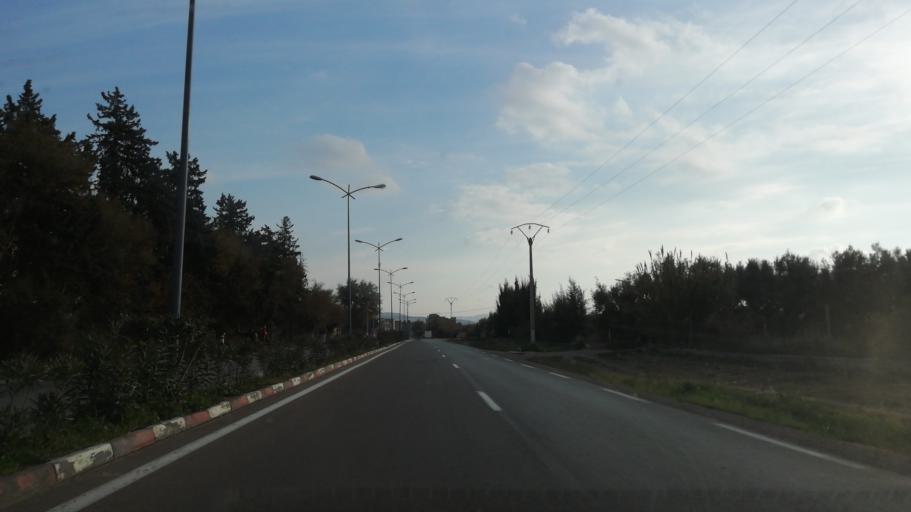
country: DZ
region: Mascara
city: Mascara
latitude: 35.6015
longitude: 0.0637
